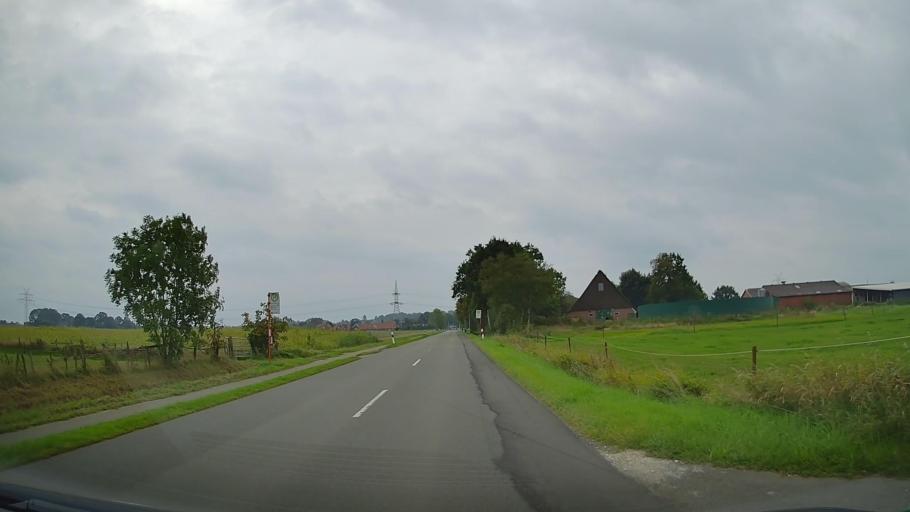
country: DE
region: Lower Saxony
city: Stade
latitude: 53.6233
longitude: 9.4639
